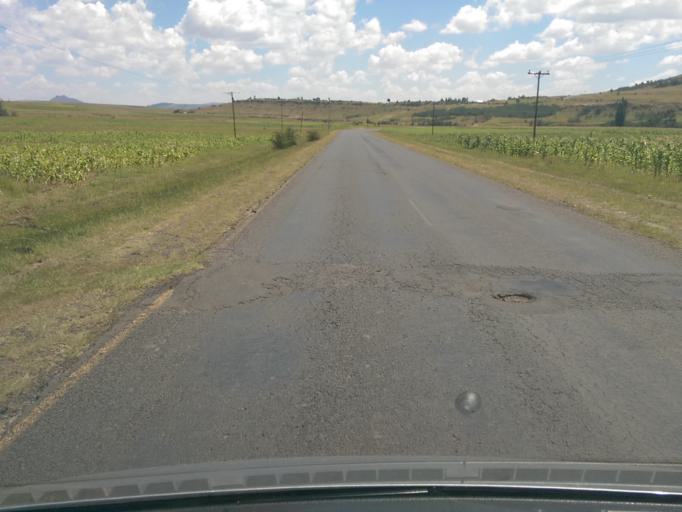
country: LS
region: Maseru
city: Nako
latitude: -29.4374
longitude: 27.6964
